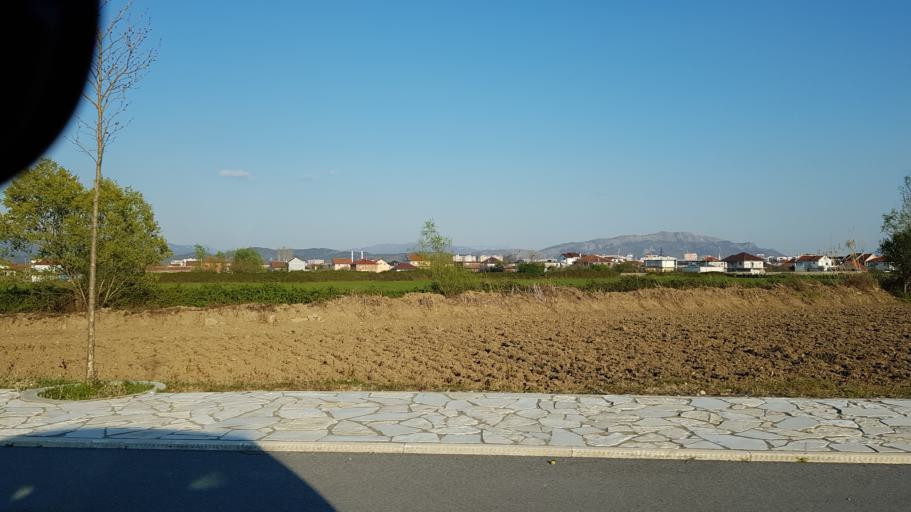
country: AL
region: Shkoder
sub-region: Rrethi i Shkodres
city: Shkoder
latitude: 42.0767
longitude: 19.4915
